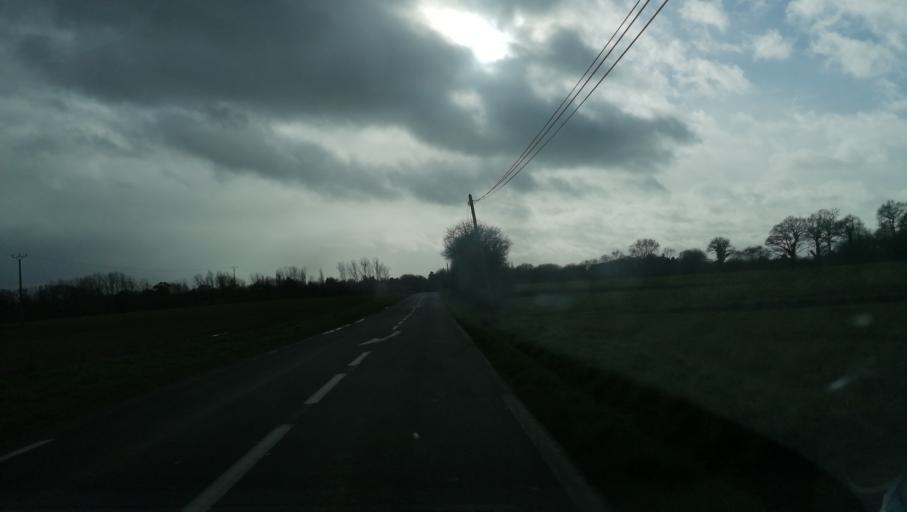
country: FR
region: Brittany
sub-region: Departement des Cotes-d'Armor
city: Lantic
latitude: 48.5871
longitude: -2.9154
